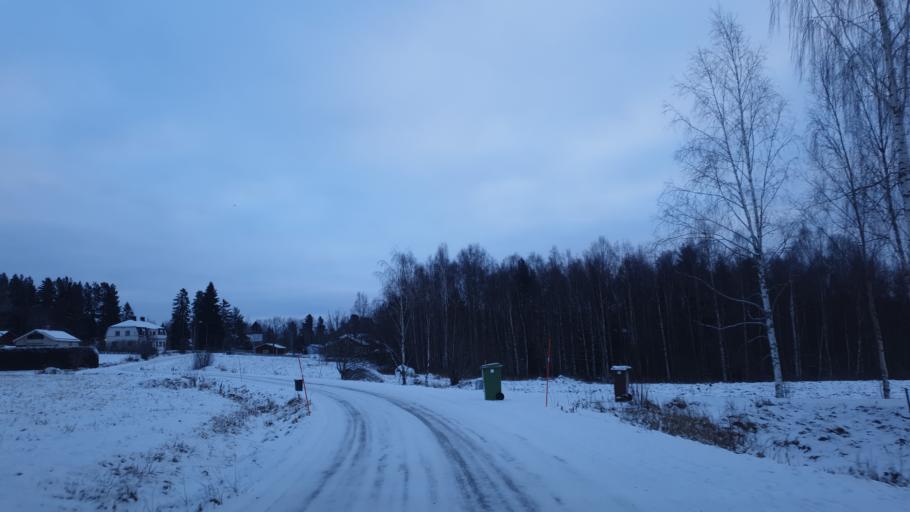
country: SE
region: Gaevleborg
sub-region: Bollnas Kommun
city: Kilafors
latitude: 61.2531
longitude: 16.5453
